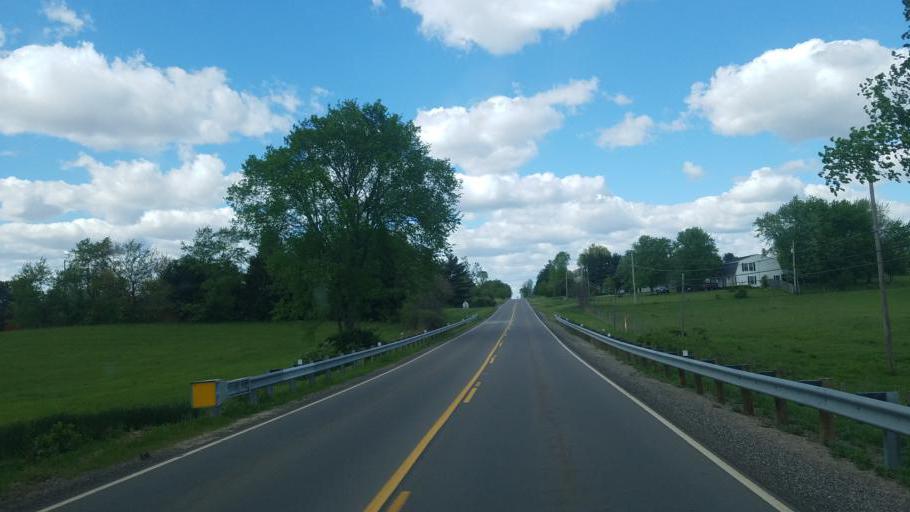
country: US
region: Ohio
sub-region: Morrow County
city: Mount Gilead
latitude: 40.5208
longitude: -82.8355
